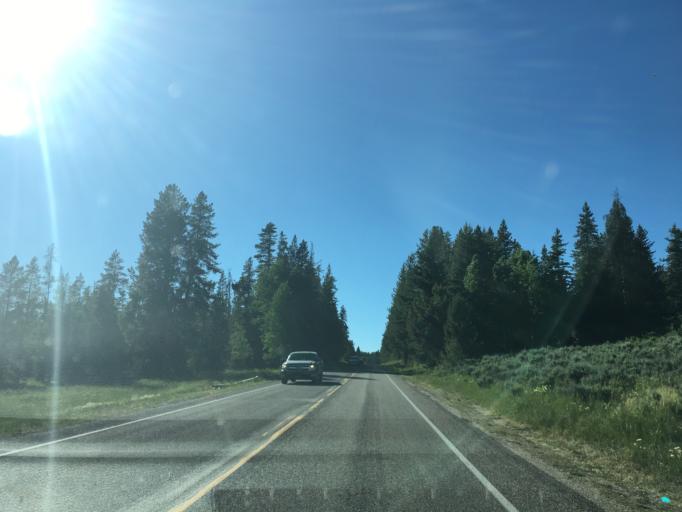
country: US
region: Wyoming
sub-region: Teton County
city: Jackson
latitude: 43.8606
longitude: -110.5321
